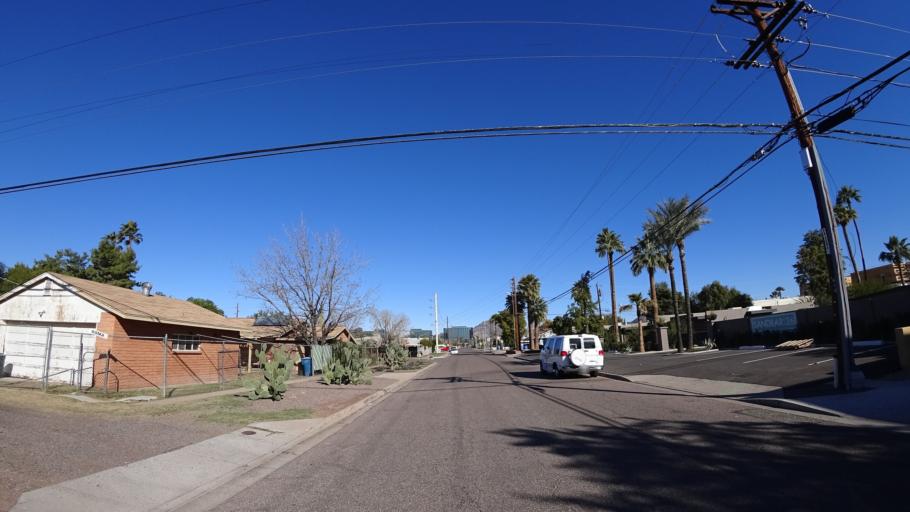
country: US
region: Arizona
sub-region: Maricopa County
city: Phoenix
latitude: 33.5008
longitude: -112.0260
